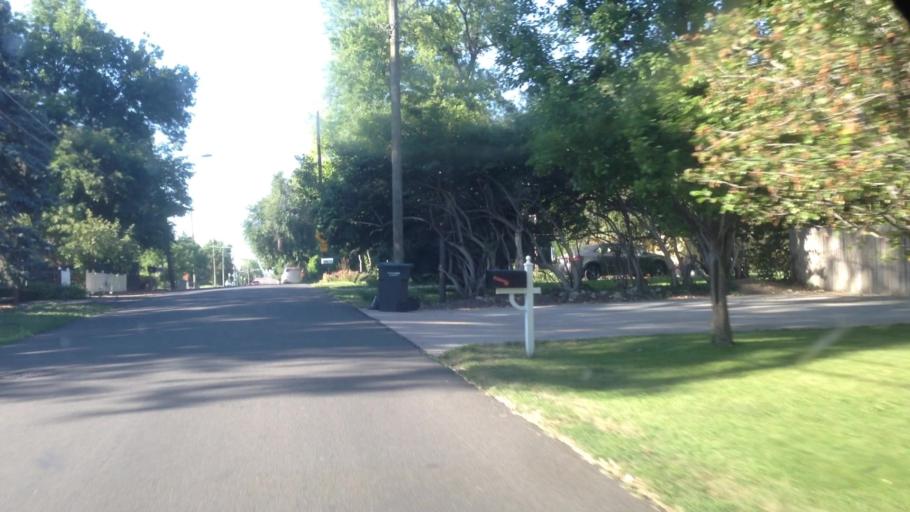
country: US
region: Colorado
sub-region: Jefferson County
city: Lakewood
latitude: 39.7214
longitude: -105.0769
